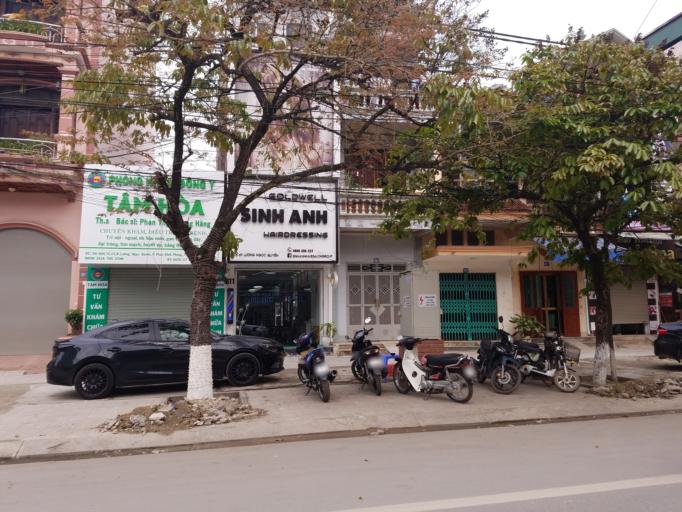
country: VN
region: Thai Nguyen
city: Thanh Pho Thai Nguyen
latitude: 21.5833
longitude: 105.8348
